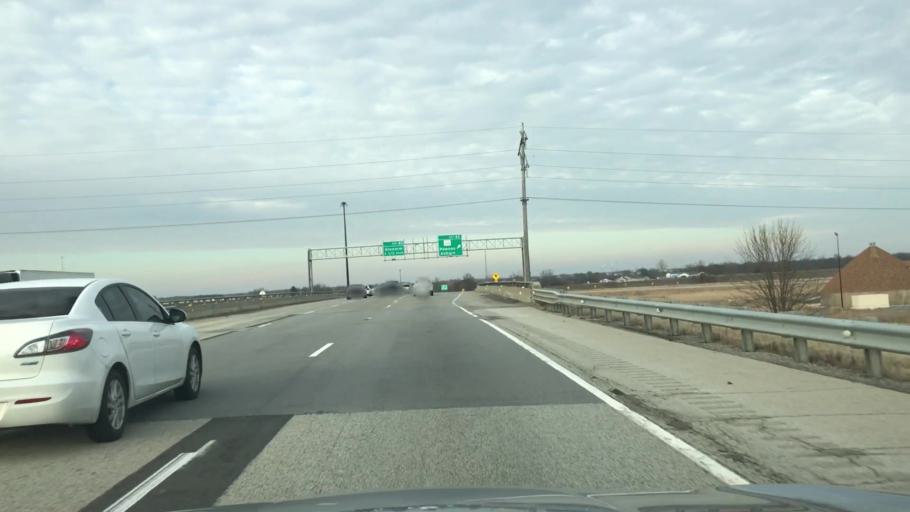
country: US
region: Illinois
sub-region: Sangamon County
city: Divernon
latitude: 39.5893
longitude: -89.6463
